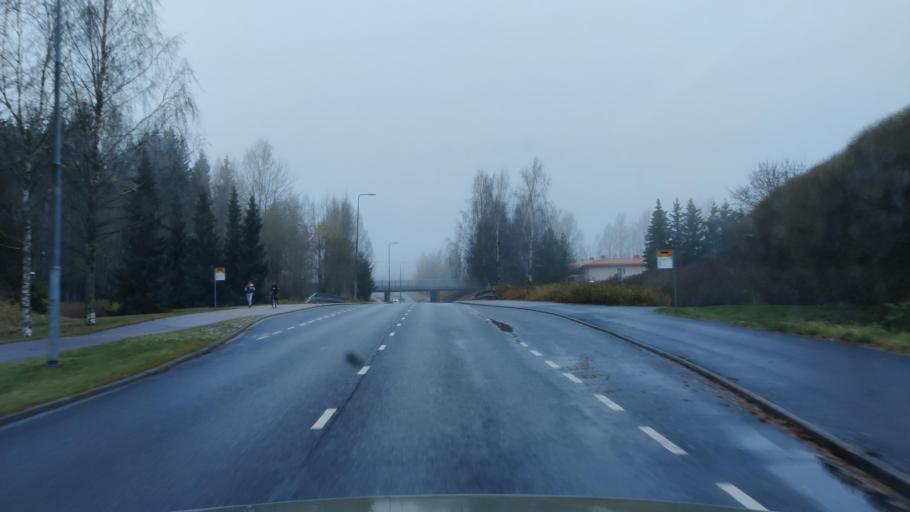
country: FI
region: Uusimaa
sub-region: Helsinki
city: Kerava
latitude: 60.3584
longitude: 25.0866
